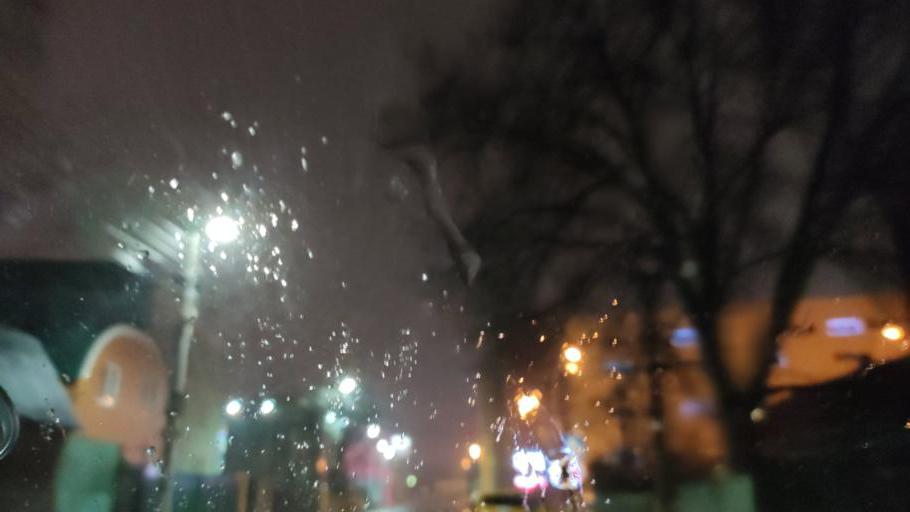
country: RU
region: Moskovskaya
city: Novoivanovskoye
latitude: 55.7137
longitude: 37.3744
